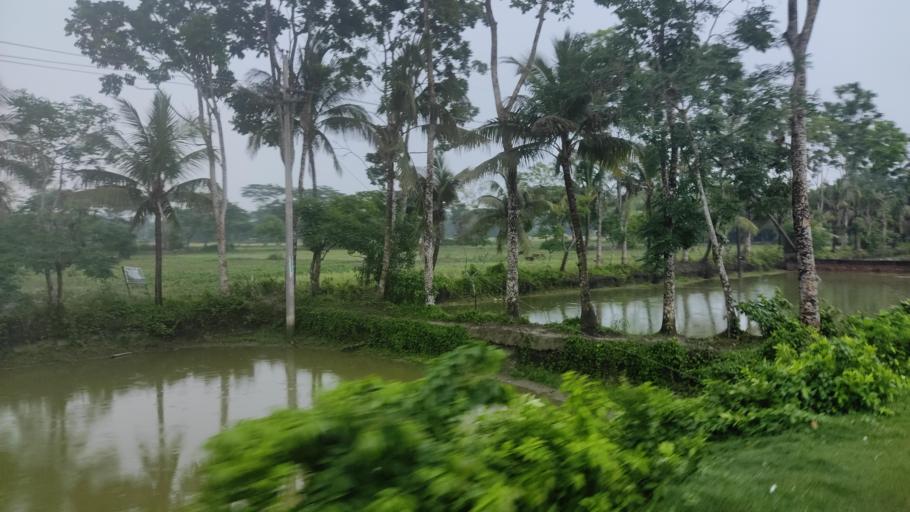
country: BD
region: Barisal
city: Bhandaria
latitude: 22.3069
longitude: 90.3247
